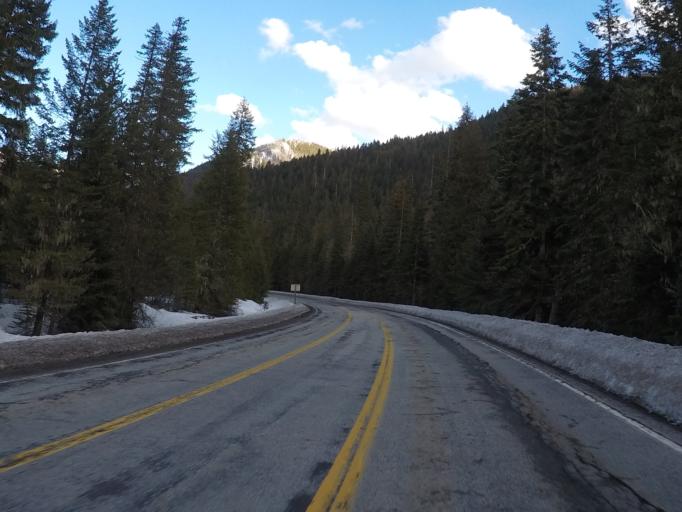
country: US
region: Montana
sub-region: Ravalli County
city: Hamilton
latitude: 46.5080
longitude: -114.7774
